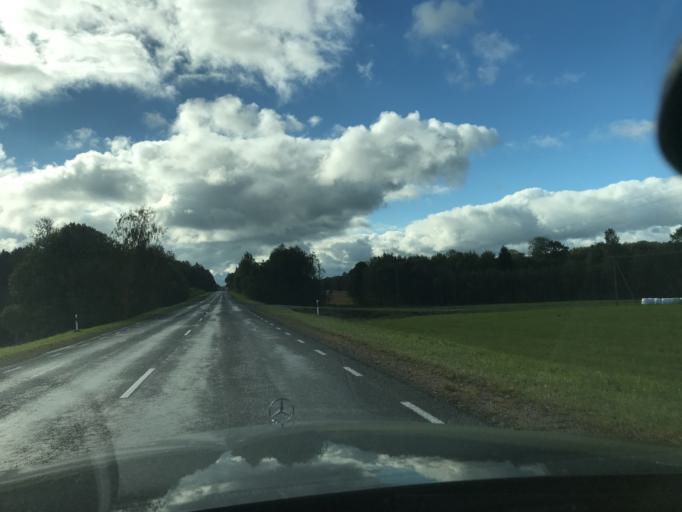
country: EE
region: Tartu
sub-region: Elva linn
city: Elva
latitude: 57.9872
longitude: 26.2623
